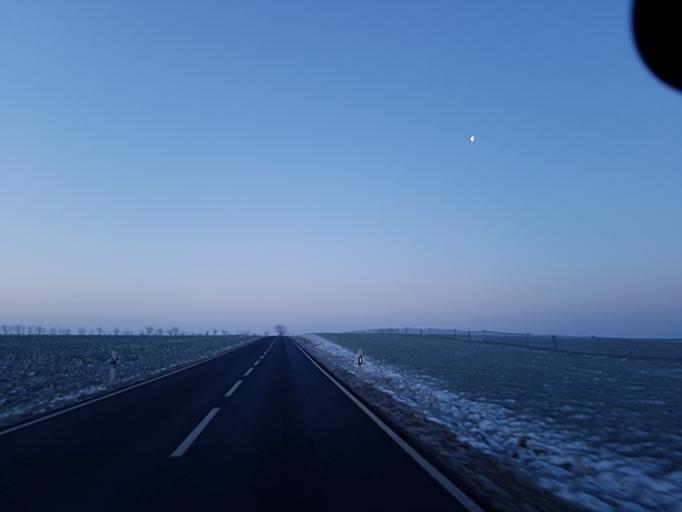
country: DE
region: Saxony
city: Strehla
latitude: 51.3402
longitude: 13.2116
